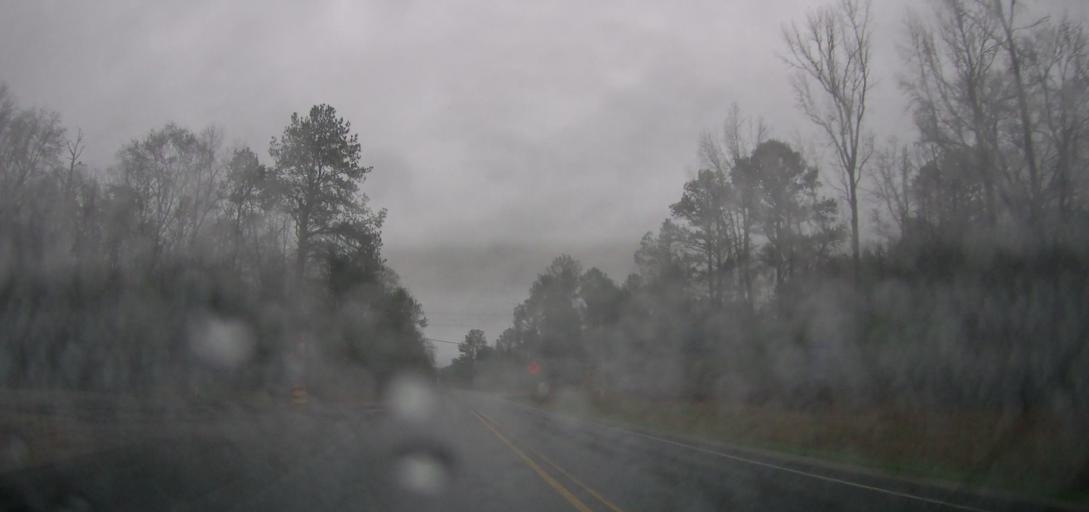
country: US
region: Alabama
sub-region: Autauga County
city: Pine Level
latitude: 32.5739
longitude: -86.6824
